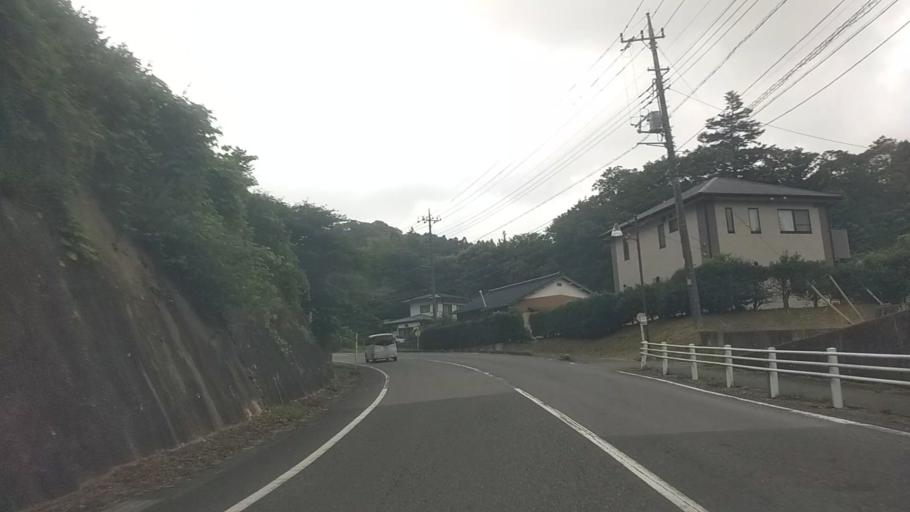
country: JP
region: Chiba
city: Kawaguchi
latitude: 35.2420
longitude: 140.1706
